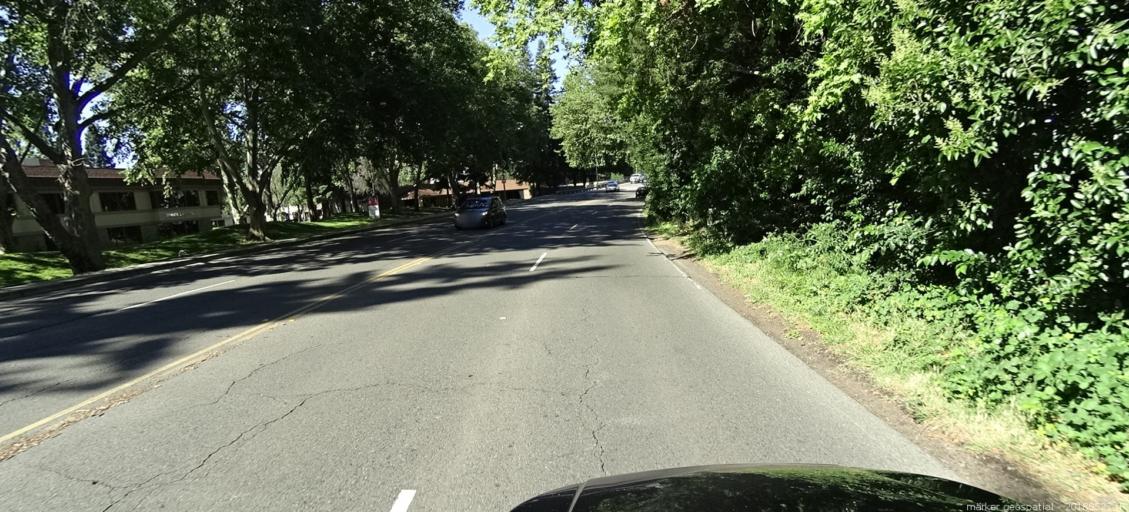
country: US
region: California
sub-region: Sacramento County
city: Arden-Arcade
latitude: 38.5697
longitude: -121.4197
